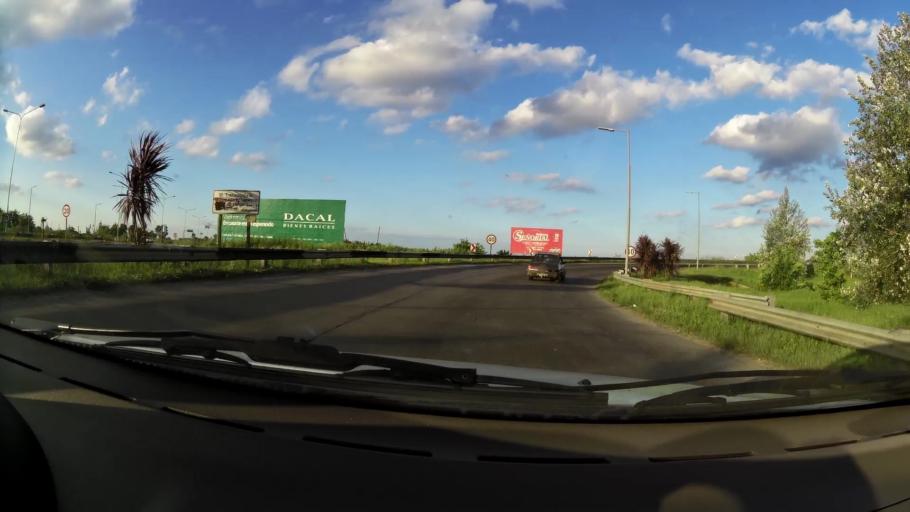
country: AR
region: Buenos Aires
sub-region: Partido de La Plata
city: La Plata
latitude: -34.8806
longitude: -57.9568
